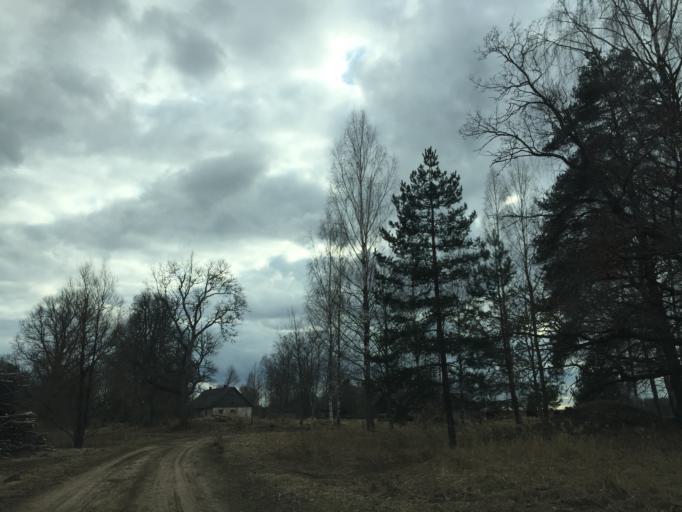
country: LV
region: Lielvarde
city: Lielvarde
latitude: 56.4888
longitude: 24.7801
